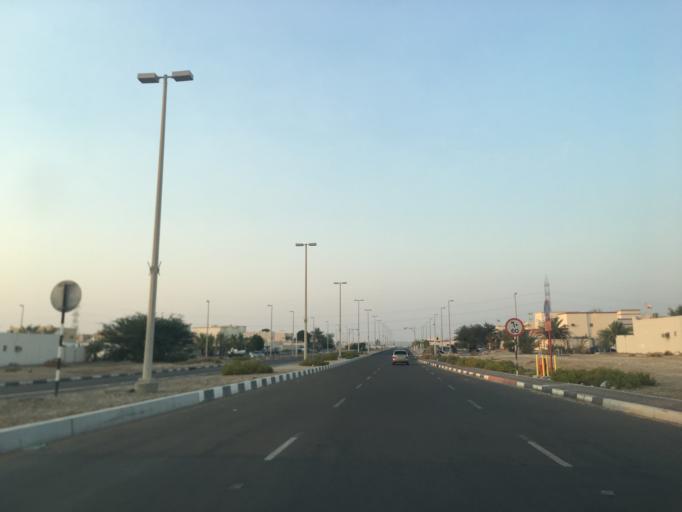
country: AE
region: Abu Dhabi
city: Abu Dhabi
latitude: 24.3003
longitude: 54.6488
